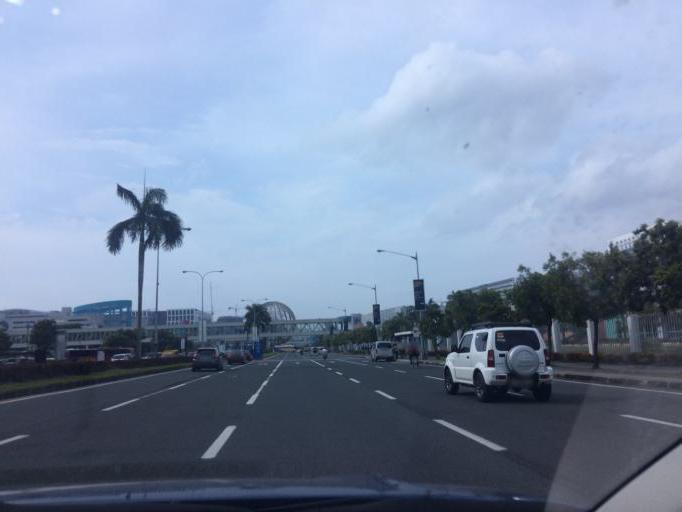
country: PH
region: Metro Manila
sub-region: Makati City
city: Makati City
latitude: 14.5322
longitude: 120.9846
